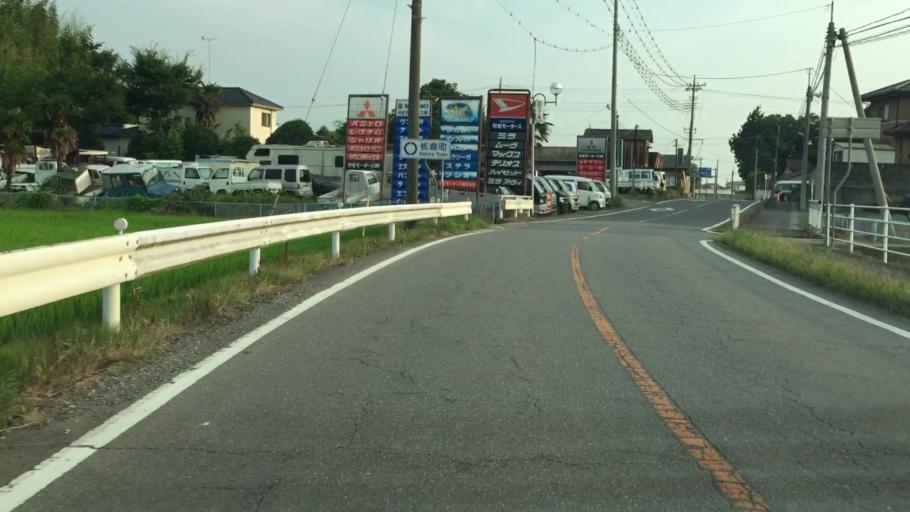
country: JP
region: Tochigi
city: Fujioka
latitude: 36.2513
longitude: 139.6197
